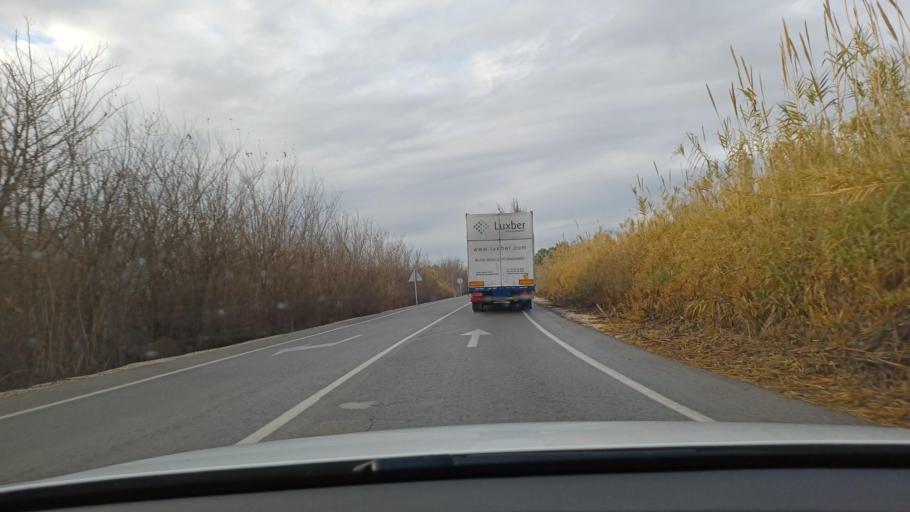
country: ES
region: Valencia
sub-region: Provincia de Alicante
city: Daya Vieja
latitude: 38.1584
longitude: -0.7041
